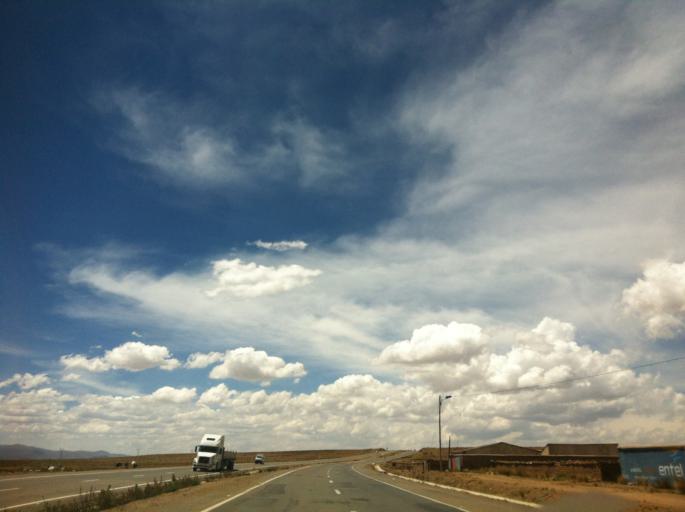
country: BO
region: La Paz
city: Patacamaya
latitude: -17.0918
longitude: -68.0089
